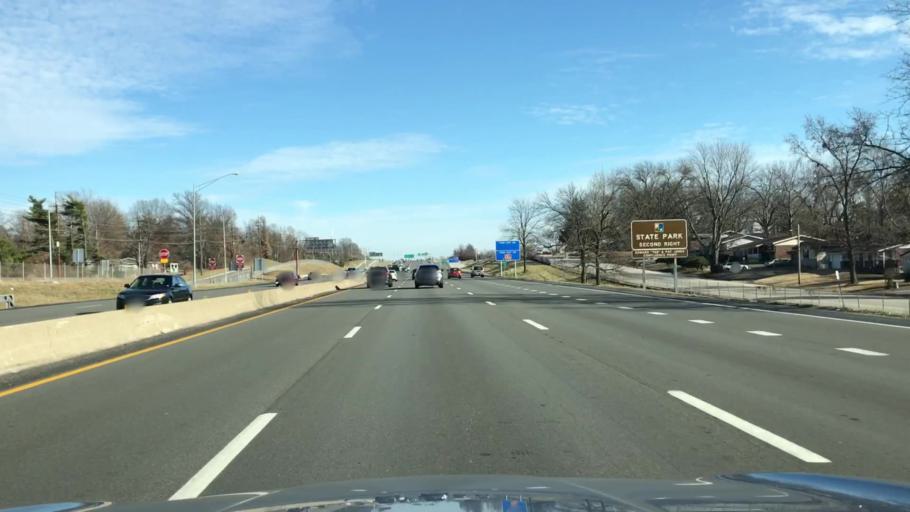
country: US
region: Missouri
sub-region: Saint Louis County
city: Castle Point
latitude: 38.7708
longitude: -90.2561
